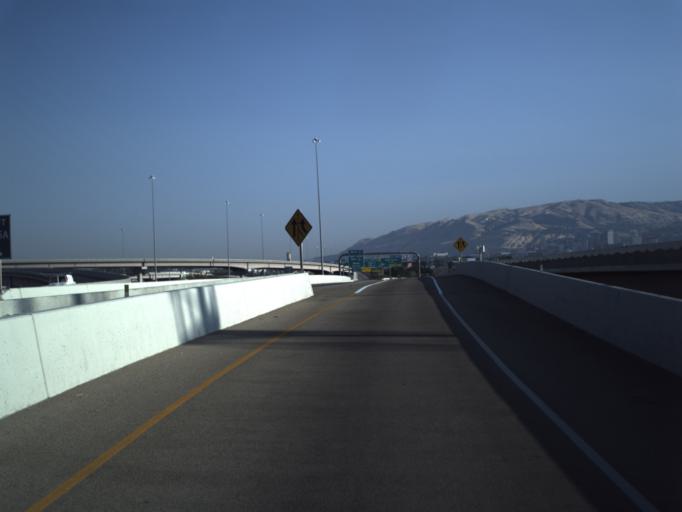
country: US
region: Utah
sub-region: Salt Lake County
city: South Salt Lake
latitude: 40.7205
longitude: -111.9033
